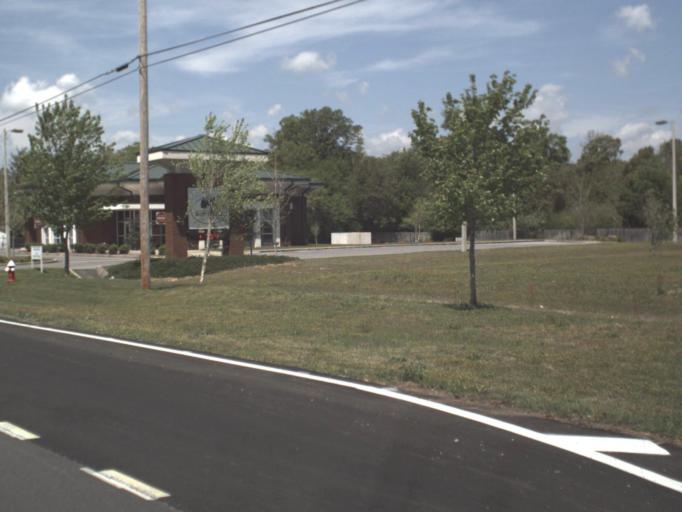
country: US
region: Florida
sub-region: Escambia County
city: Ensley
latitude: 30.5338
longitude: -87.2925
